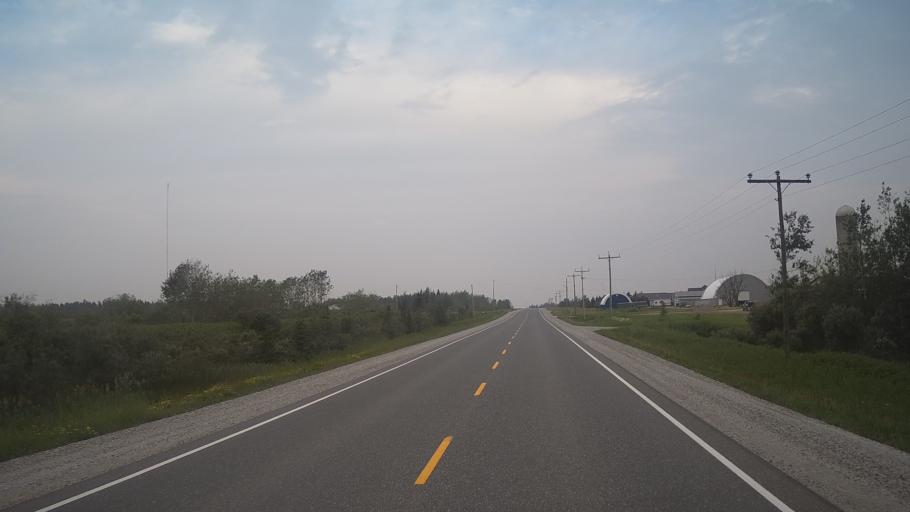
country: CA
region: Ontario
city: Hearst
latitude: 49.6654
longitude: -83.4956
